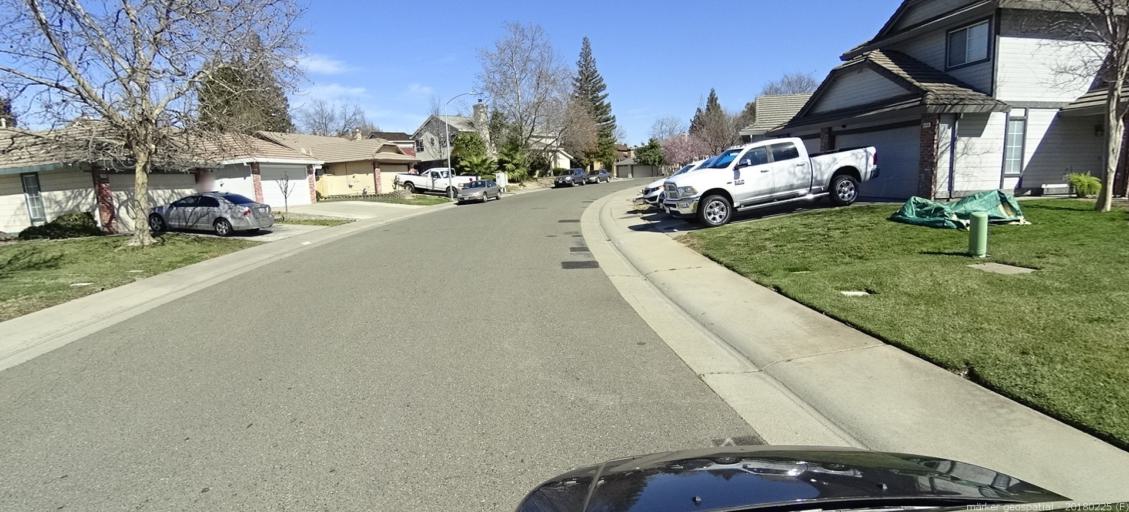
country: US
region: California
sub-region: Sacramento County
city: Antelope
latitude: 38.7202
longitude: -121.3536
